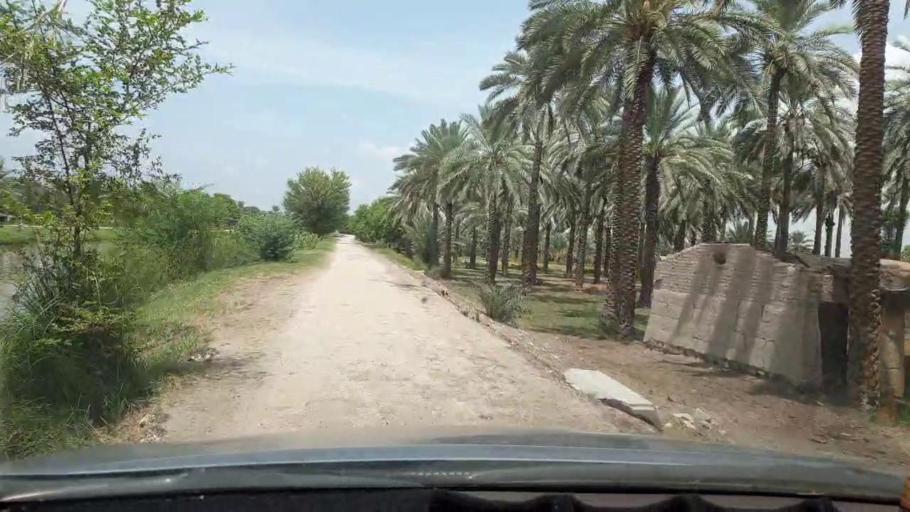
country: PK
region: Sindh
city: Khairpur
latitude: 27.4573
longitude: 68.8010
